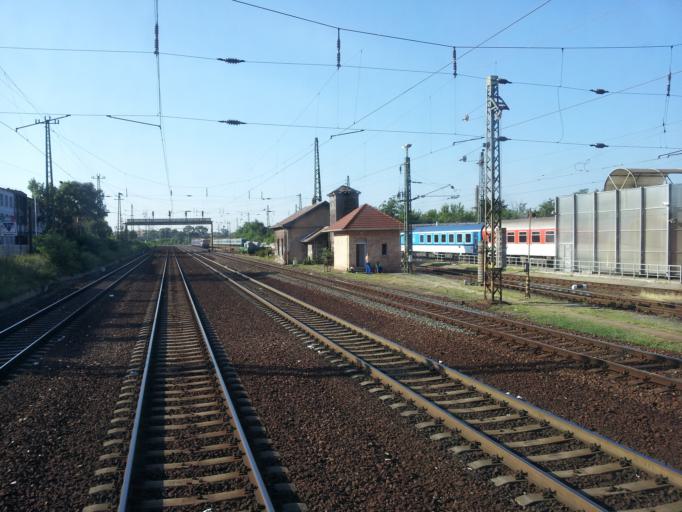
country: HU
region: Budapest
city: Budapest XIV. keruelet
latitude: 47.4953
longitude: 19.1007
